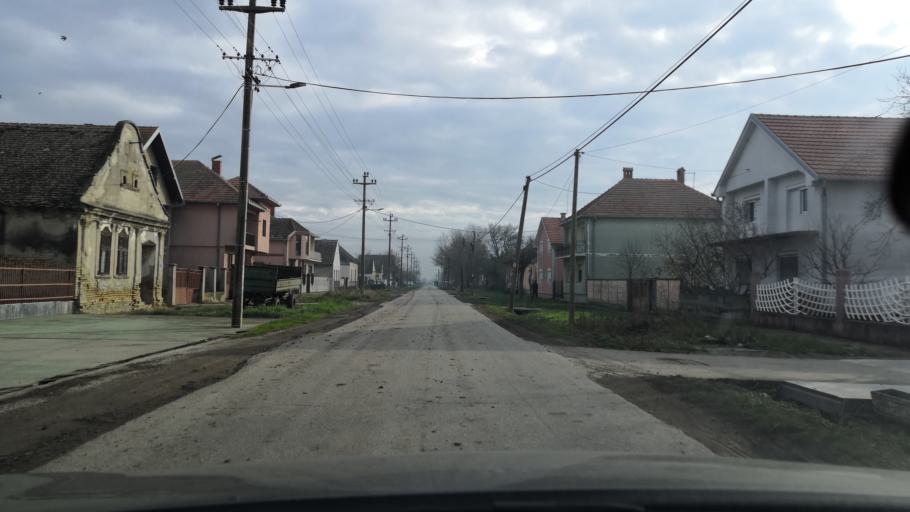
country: RS
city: Ugrinovci
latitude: 44.8888
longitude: 20.1405
